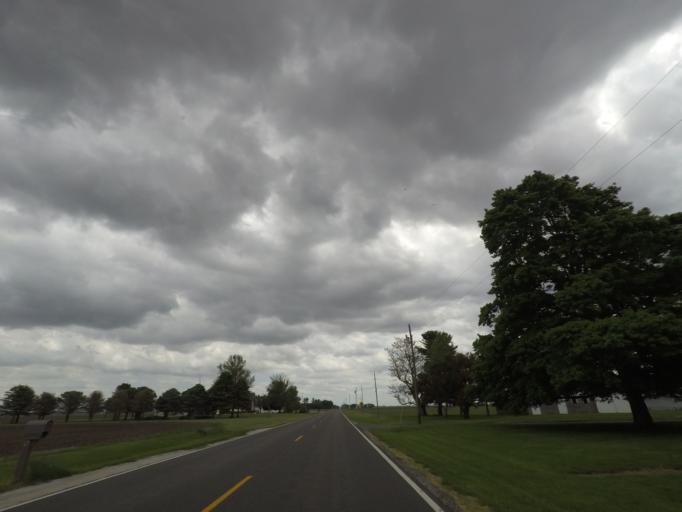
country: US
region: Illinois
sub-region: Macon County
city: Warrensburg
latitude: 39.9941
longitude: -89.0857
